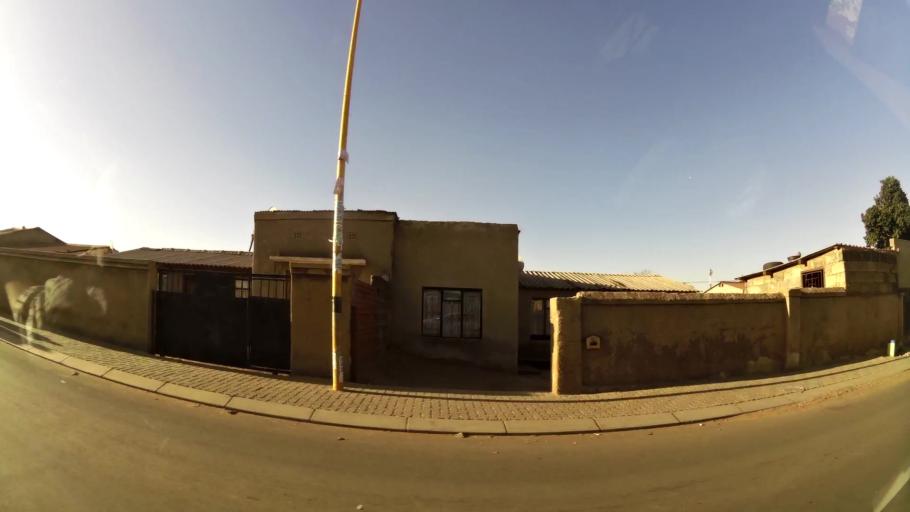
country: ZA
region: Gauteng
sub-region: Ekurhuleni Metropolitan Municipality
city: Tembisa
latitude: -26.0099
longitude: 28.2261
